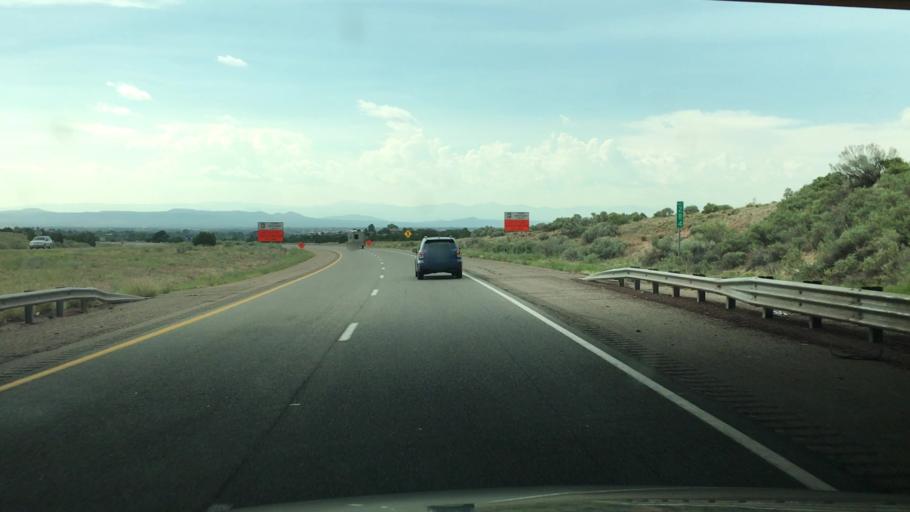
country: US
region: New Mexico
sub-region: Santa Fe County
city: Santa Fe
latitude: 35.6367
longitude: -105.9304
